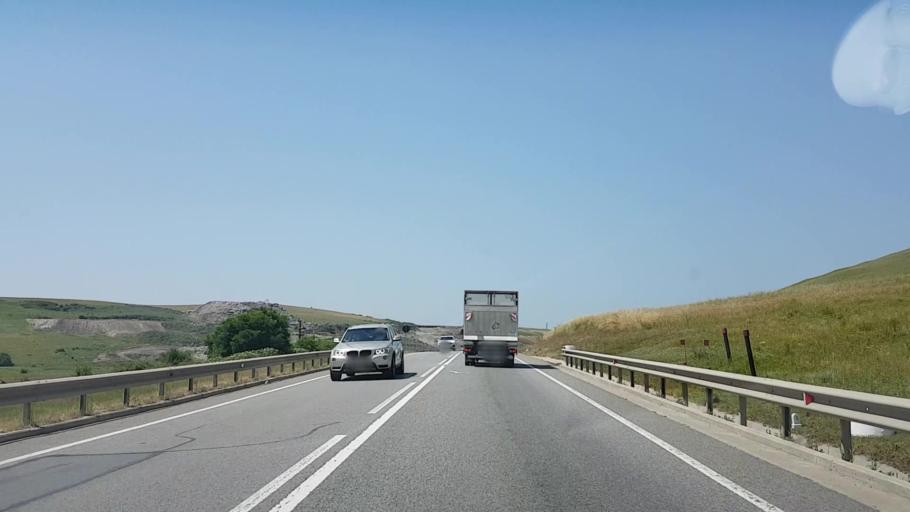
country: RO
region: Cluj
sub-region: Comuna Apahida
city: Dezmir
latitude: 46.7590
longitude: 23.6957
